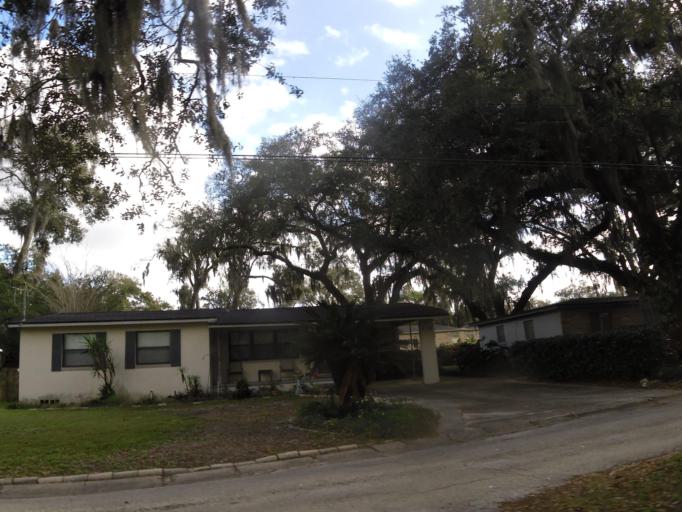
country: US
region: Florida
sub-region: Duval County
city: Jacksonville
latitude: 30.3414
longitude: -81.6001
